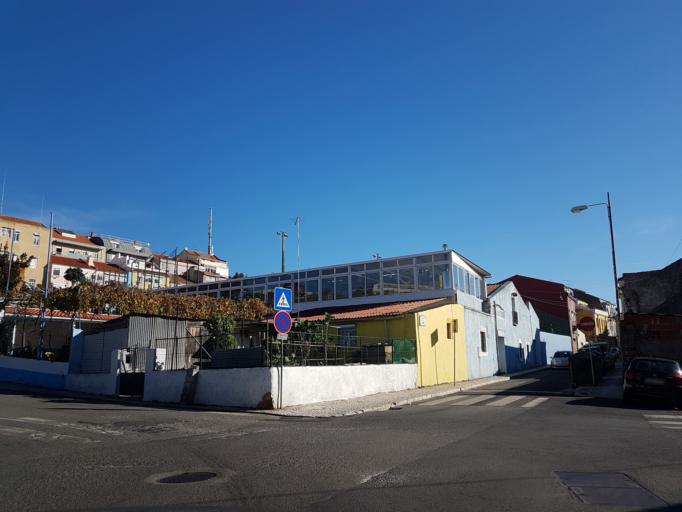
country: PT
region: Lisbon
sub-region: Oeiras
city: Alges
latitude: 38.7093
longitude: -9.1950
